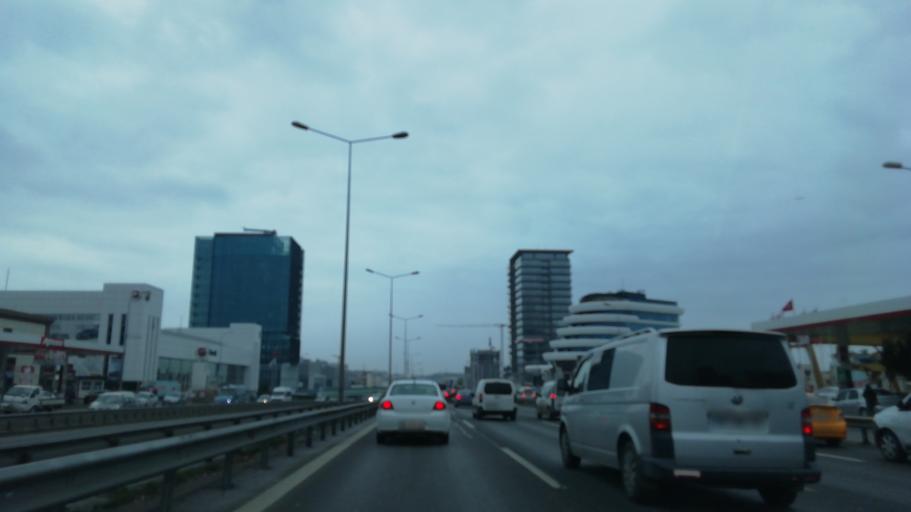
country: TR
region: Istanbul
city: Pendik
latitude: 40.8972
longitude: 29.2249
